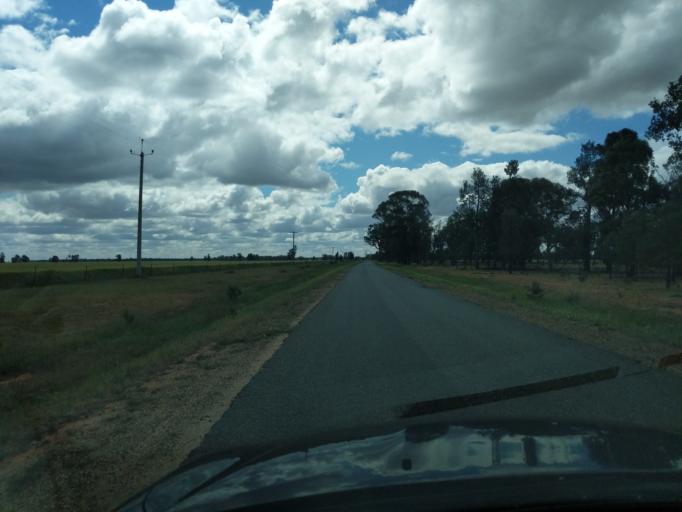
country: AU
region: New South Wales
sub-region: Coolamon
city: Coolamon
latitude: -34.8643
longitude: 146.8971
